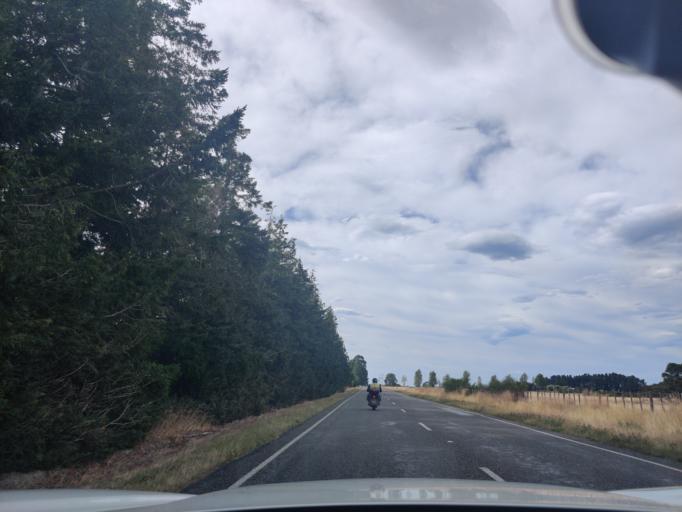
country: NZ
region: Wellington
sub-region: Masterton District
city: Masterton
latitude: -40.8718
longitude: 175.6495
